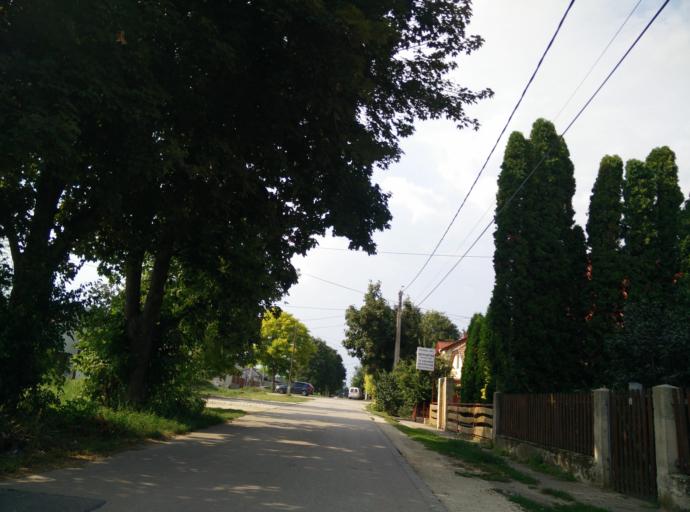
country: HU
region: Pest
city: Paty
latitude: 47.5187
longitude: 18.8238
